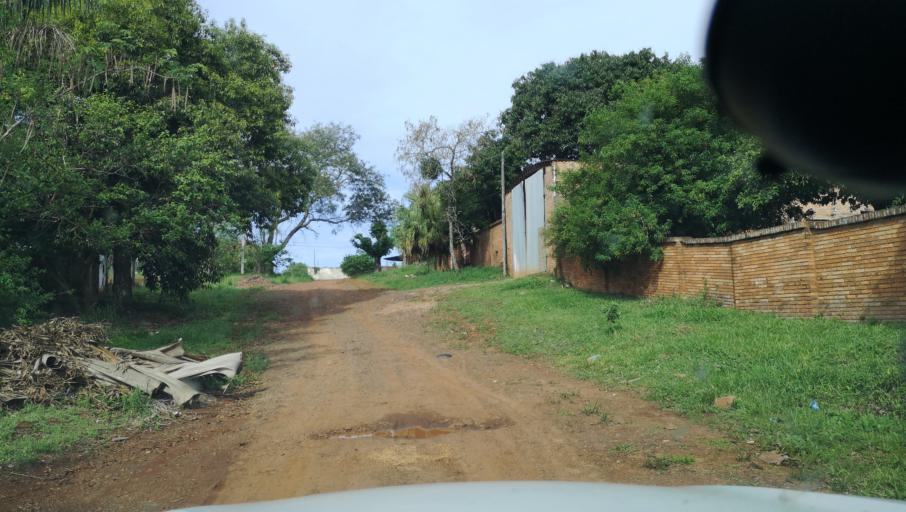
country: PY
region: Itapua
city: Carmen del Parana
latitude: -27.1619
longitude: -56.2327
